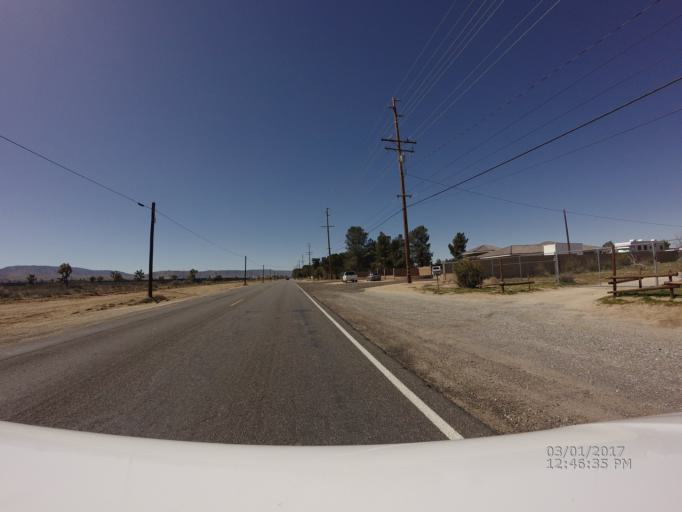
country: US
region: California
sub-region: Los Angeles County
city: Desert View Highlands
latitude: 34.6458
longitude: -118.1587
